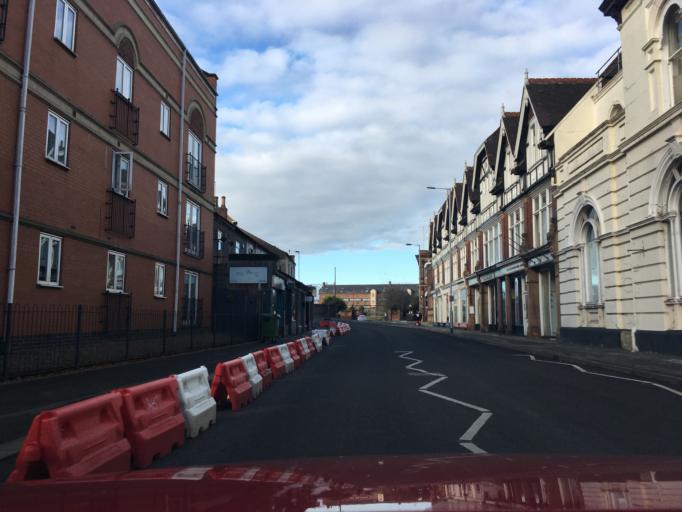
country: GB
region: England
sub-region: Staffordshire
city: Burton upon Trent
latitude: 52.8058
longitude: -1.6387
